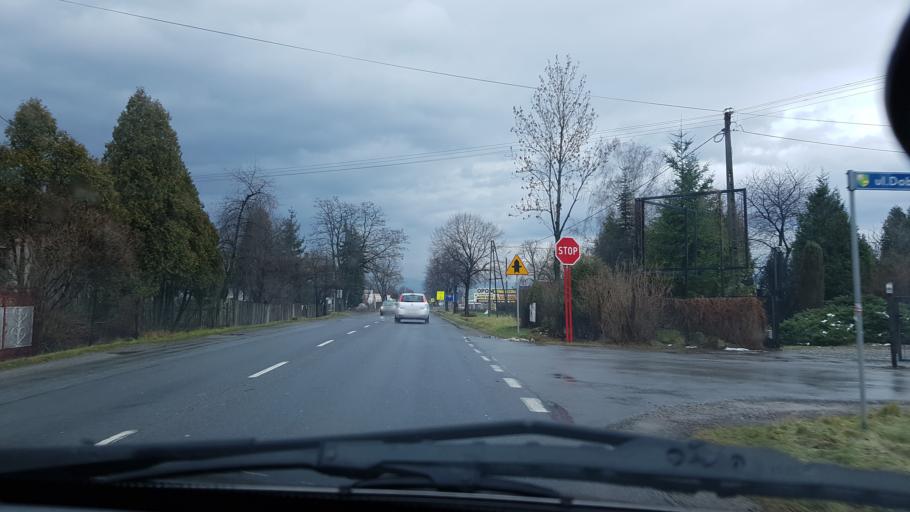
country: PL
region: Silesian Voivodeship
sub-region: Powiat zywiecki
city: Lodygowice
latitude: 49.7209
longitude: 19.1455
